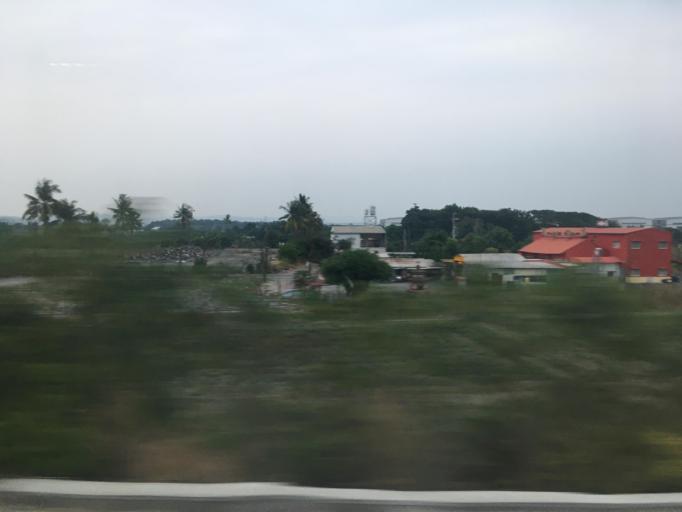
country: TW
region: Taiwan
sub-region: Pingtung
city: Pingtung
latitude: 22.6620
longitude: 120.4502
